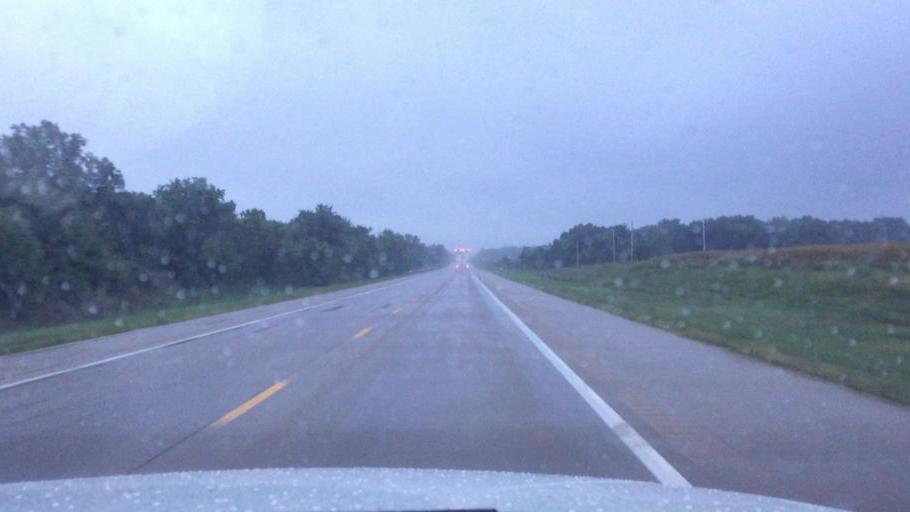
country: US
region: Kansas
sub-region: Neosho County
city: Chanute
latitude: 37.5598
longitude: -95.4709
